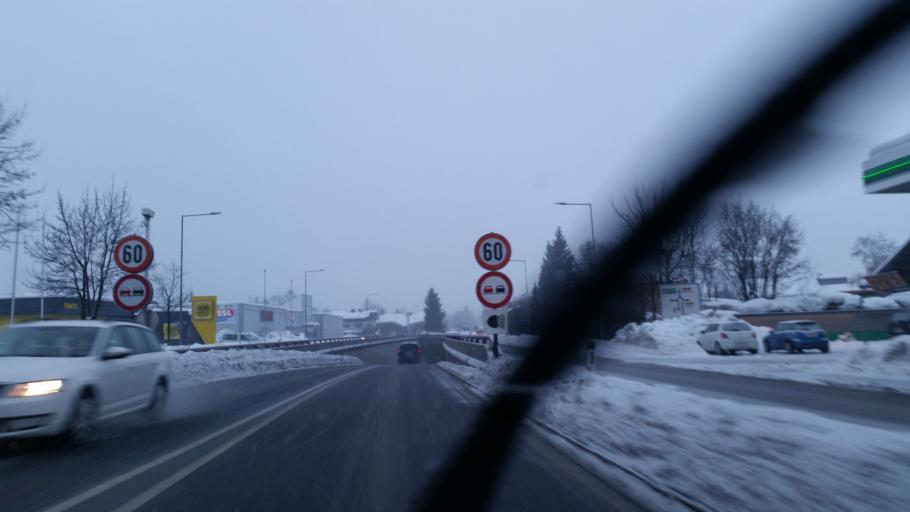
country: AT
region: Tyrol
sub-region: Politischer Bezirk Kitzbuhel
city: Sankt Johann in Tirol
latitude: 47.5254
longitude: 12.4234
